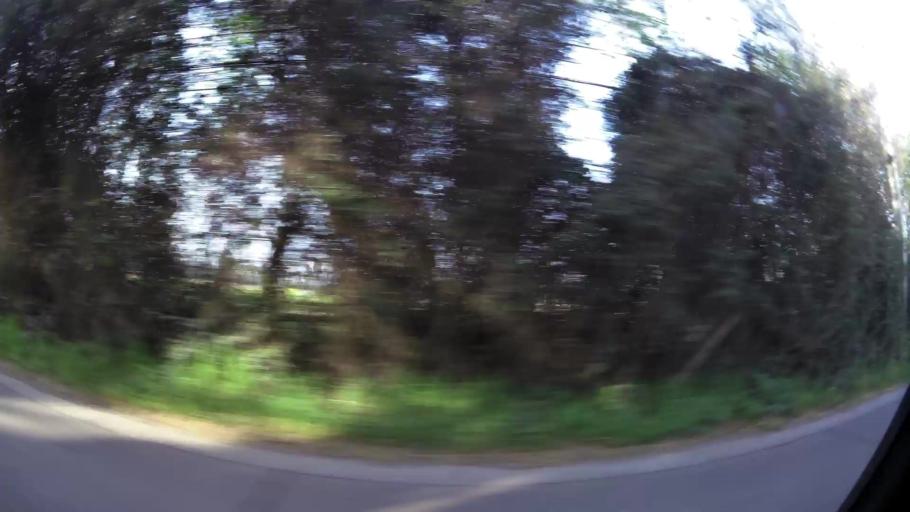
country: CL
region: Santiago Metropolitan
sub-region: Provincia de Maipo
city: San Bernardo
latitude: -33.5594
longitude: -70.7694
